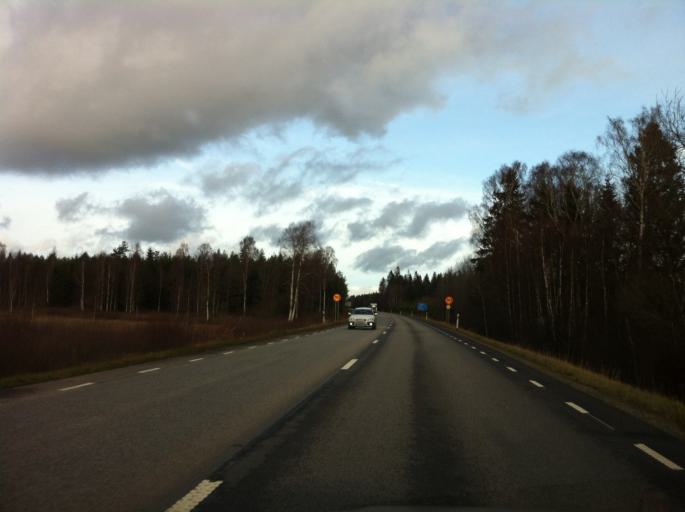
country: SE
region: Kronoberg
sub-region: Almhults Kommun
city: AElmhult
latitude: 56.5484
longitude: 14.1624
